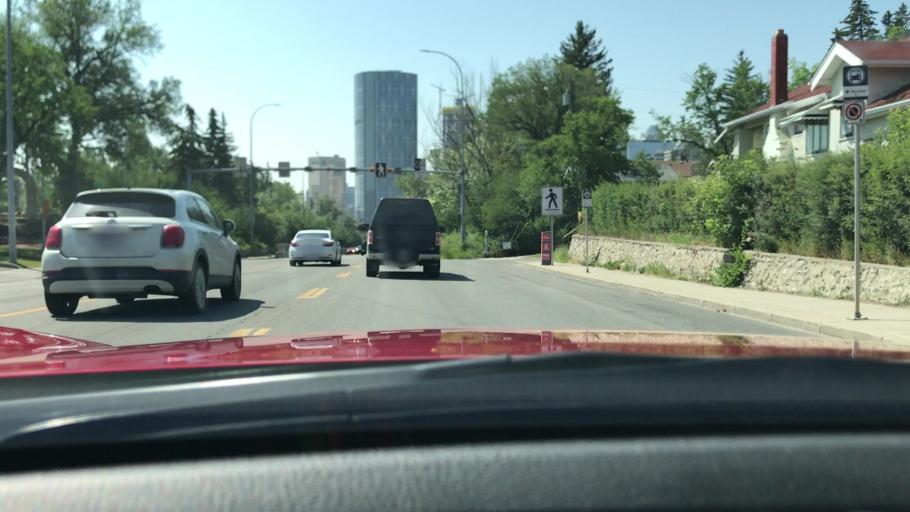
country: CA
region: Alberta
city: Calgary
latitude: 51.0593
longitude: -114.0626
